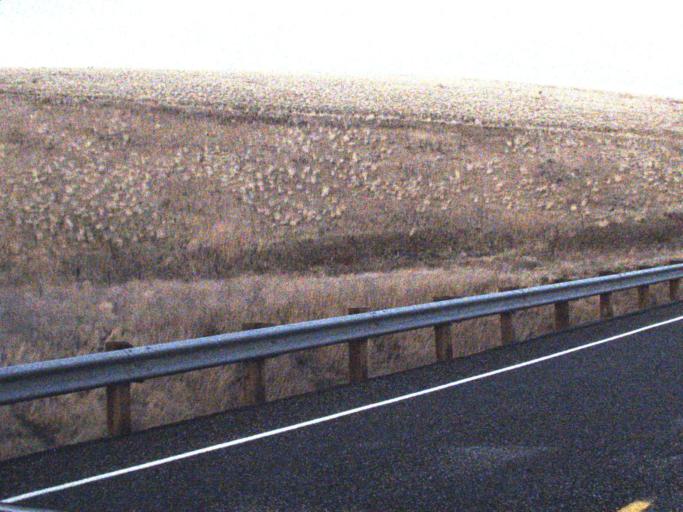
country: US
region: Washington
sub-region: Garfield County
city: Pomeroy
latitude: 46.5256
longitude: -117.8029
